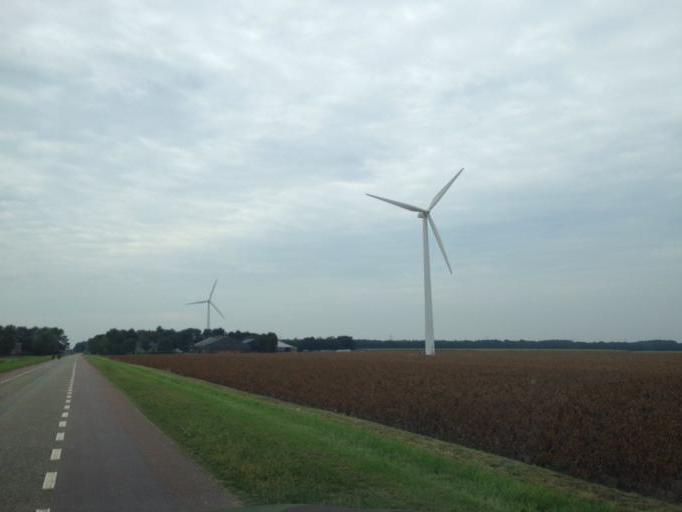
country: NL
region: Flevoland
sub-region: Gemeente Lelystad
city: Lelystad
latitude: 52.4116
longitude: 5.4141
